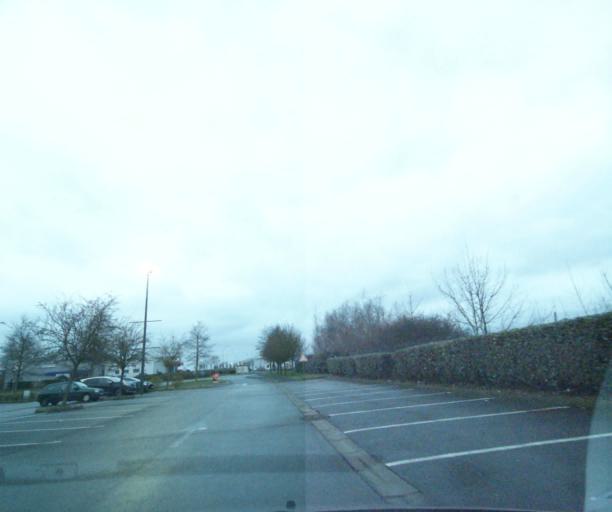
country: FR
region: Picardie
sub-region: Departement de l'Oise
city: Noyon
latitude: 49.5705
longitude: 2.9754
